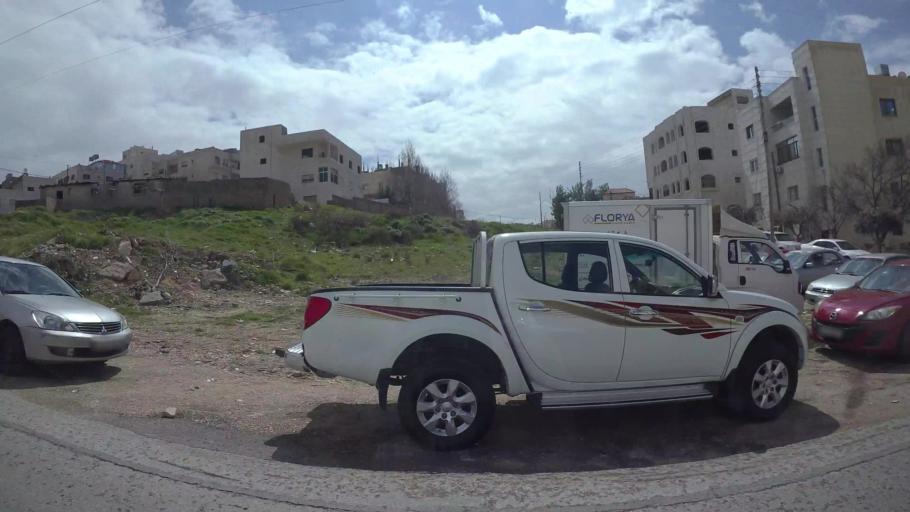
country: JO
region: Amman
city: Al Jubayhah
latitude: 31.9964
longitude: 35.8501
